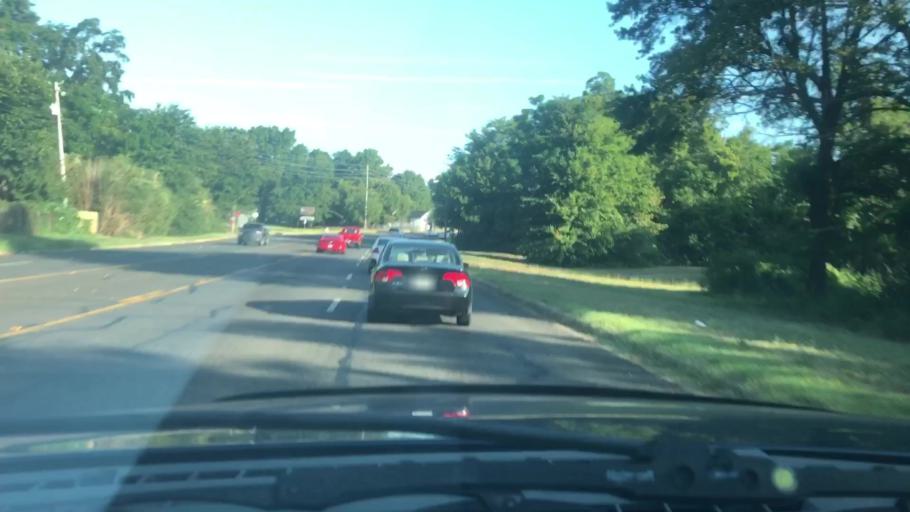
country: US
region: Texas
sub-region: Bowie County
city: Texarkana
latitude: 33.4380
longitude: -94.0630
